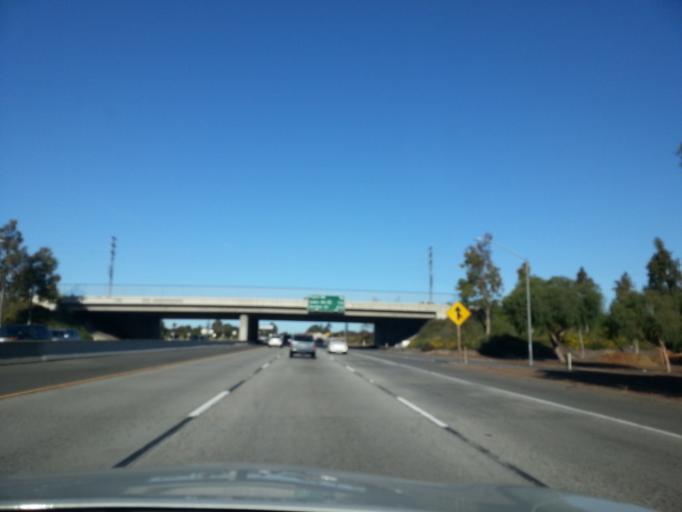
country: US
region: California
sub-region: Ventura County
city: Camarillo
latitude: 34.2134
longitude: -119.0066
